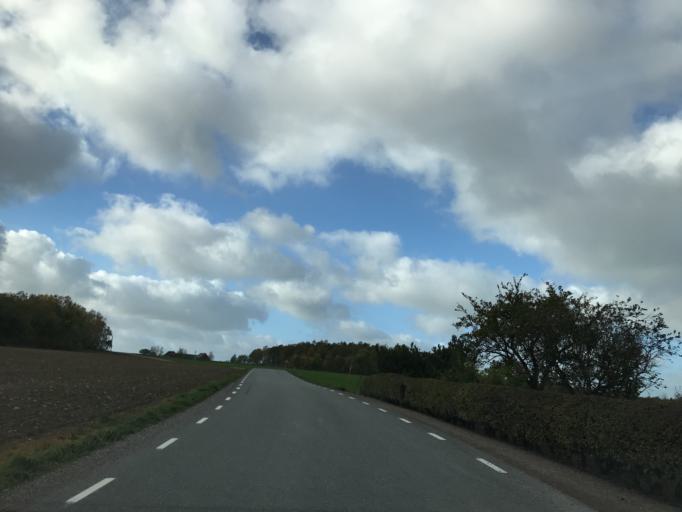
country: SE
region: Skane
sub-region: Bjuvs Kommun
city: Billesholm
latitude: 56.0124
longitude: 12.9832
